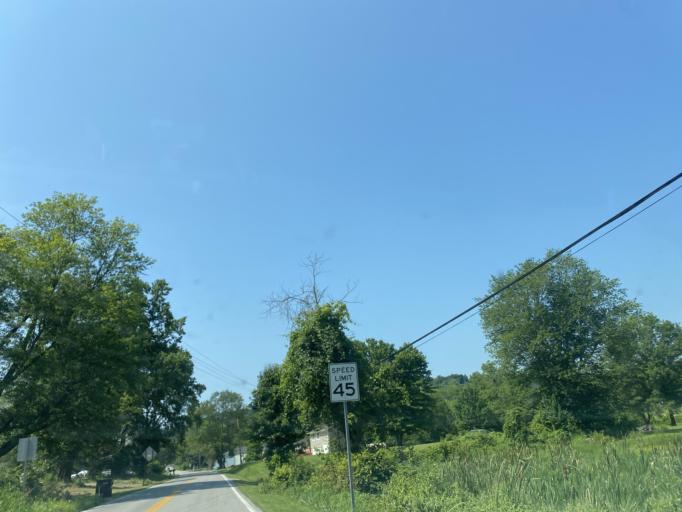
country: US
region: Kentucky
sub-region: Campbell County
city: Claryville
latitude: 38.8699
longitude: -84.4553
